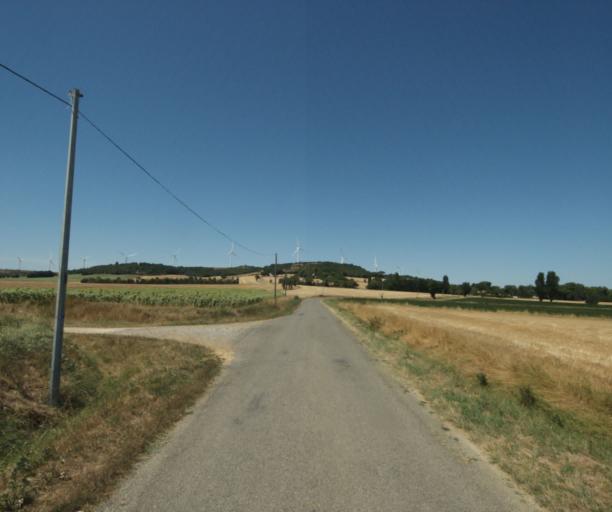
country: FR
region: Midi-Pyrenees
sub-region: Departement de la Haute-Garonne
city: Saint-Felix-Lauragais
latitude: 43.4564
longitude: 1.9302
